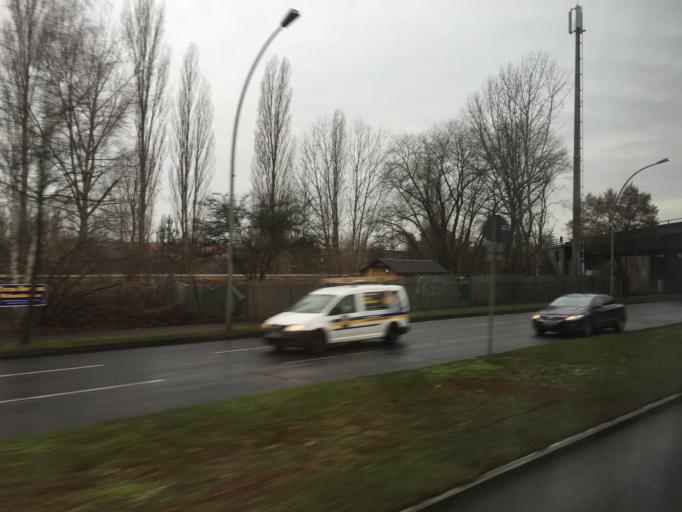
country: DE
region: Berlin
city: Niederschoneweide
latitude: 52.4493
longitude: 13.5210
